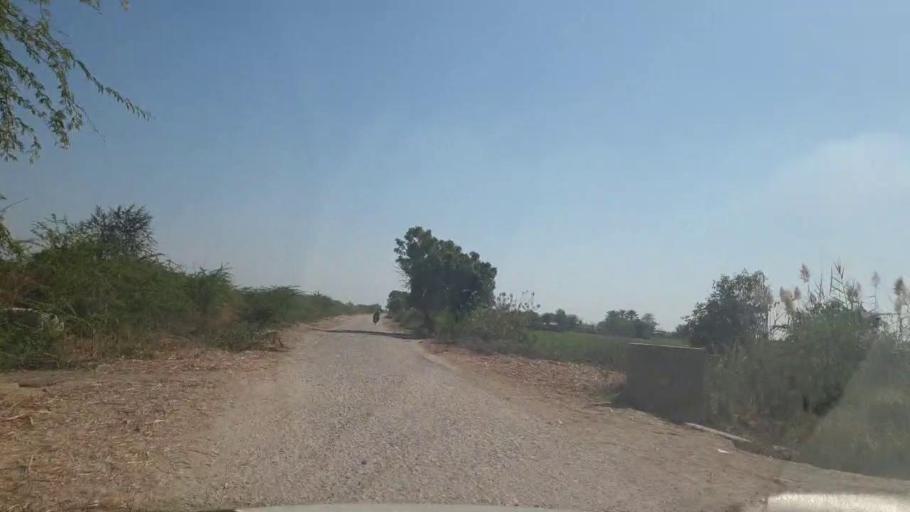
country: PK
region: Sindh
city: Mirpur Khas
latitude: 25.4884
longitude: 69.1684
